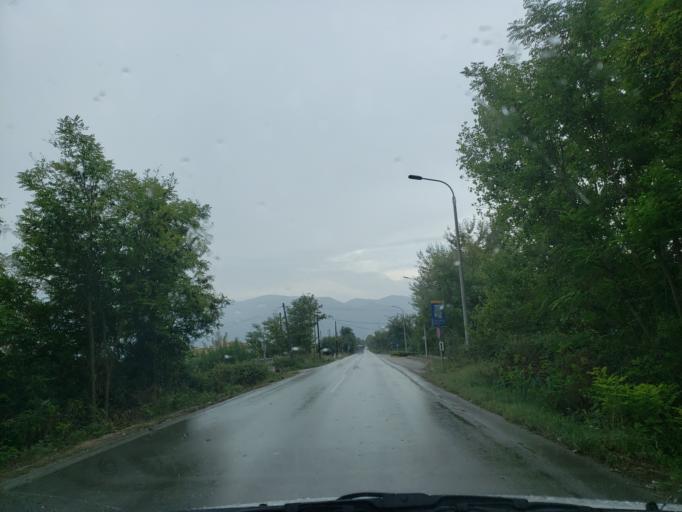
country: GR
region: Central Greece
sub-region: Nomos Fthiotidos
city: Anthili
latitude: 38.8349
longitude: 22.4412
